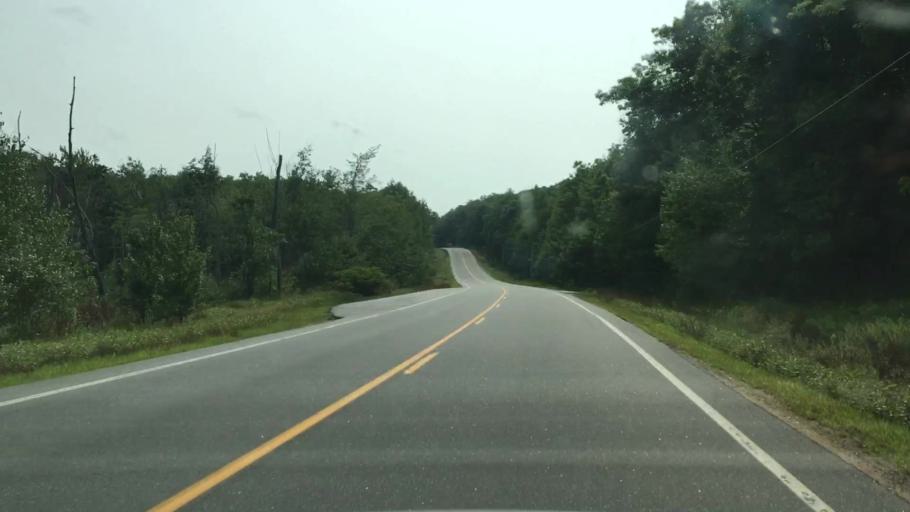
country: US
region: Maine
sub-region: Oxford County
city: Paris
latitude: 44.2612
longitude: -70.4353
